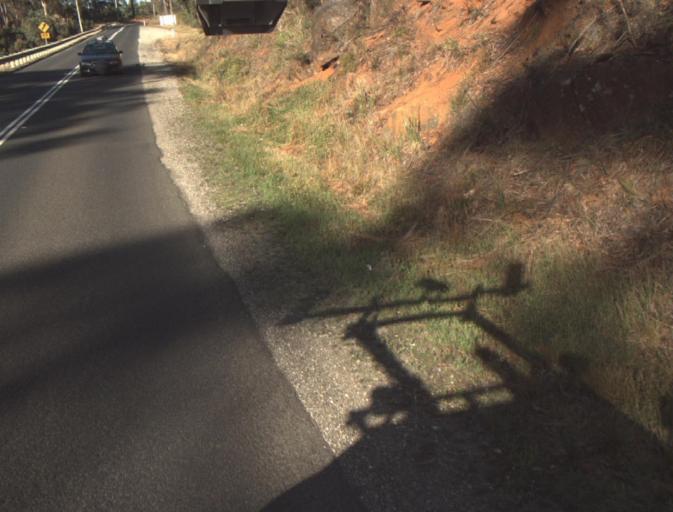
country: AU
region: Tasmania
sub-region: Launceston
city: Mayfield
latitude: -41.3356
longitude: 147.1776
